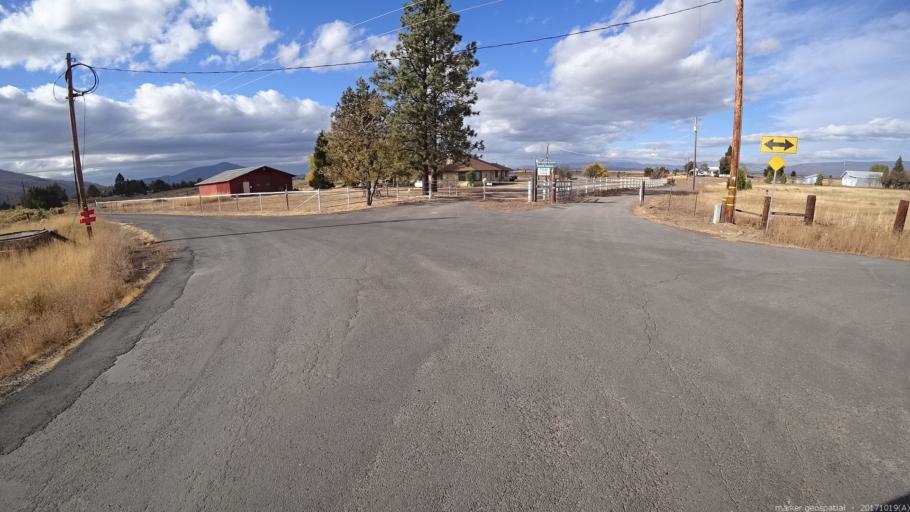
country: US
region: California
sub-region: Shasta County
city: Burney
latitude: 41.0216
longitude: -121.4370
